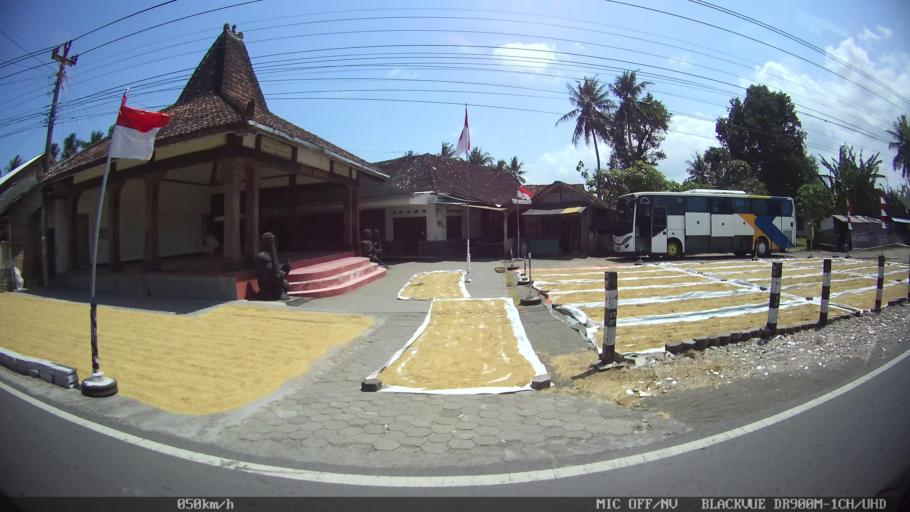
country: ID
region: Daerah Istimewa Yogyakarta
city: Srandakan
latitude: -7.9325
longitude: 110.2643
